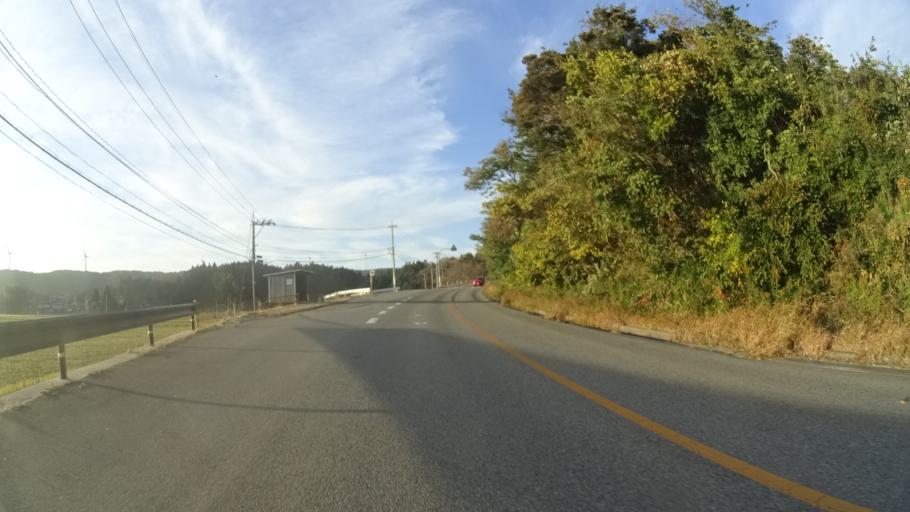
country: JP
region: Ishikawa
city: Nanao
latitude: 37.1647
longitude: 136.7143
